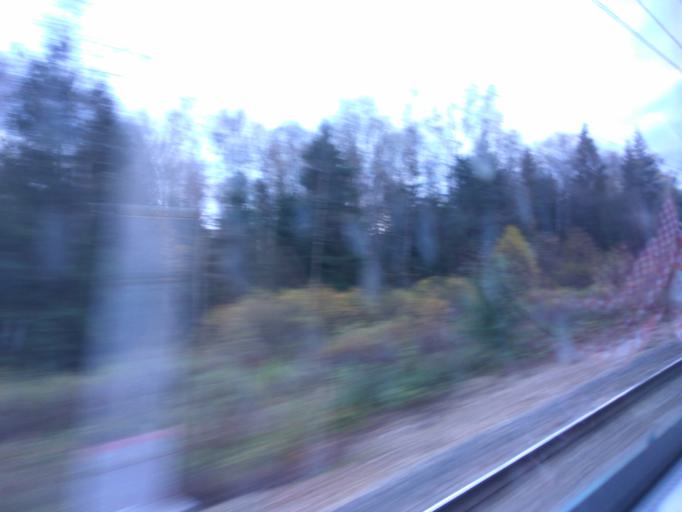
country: RU
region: Moskovskaya
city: Selyatino
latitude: 55.5023
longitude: 36.9426
